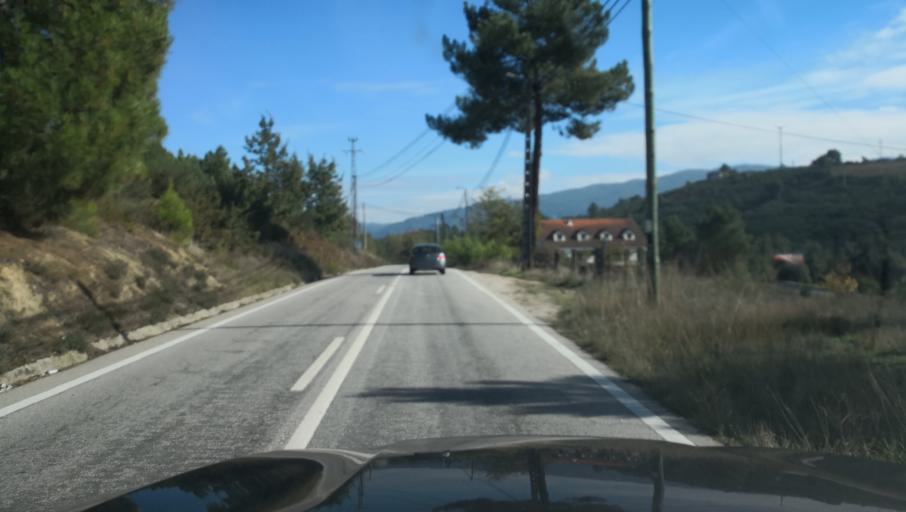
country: PT
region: Vila Real
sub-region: Chaves
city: Chaves
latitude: 41.7204
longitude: -7.4931
